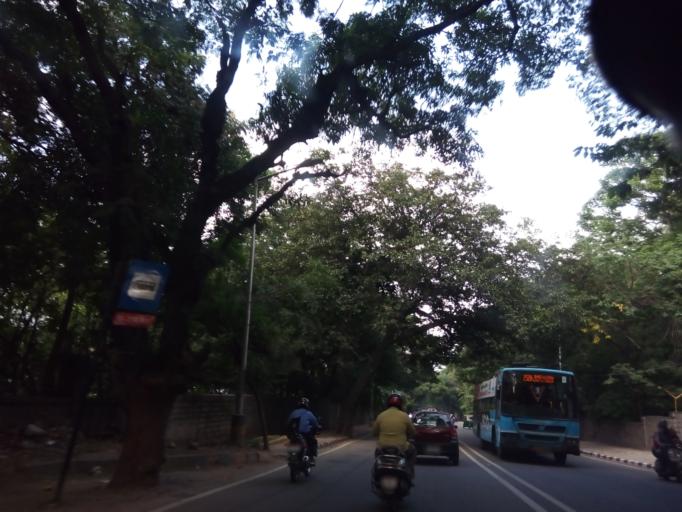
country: IN
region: Karnataka
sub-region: Bangalore Urban
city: Bangalore
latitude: 13.0143
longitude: 77.5687
